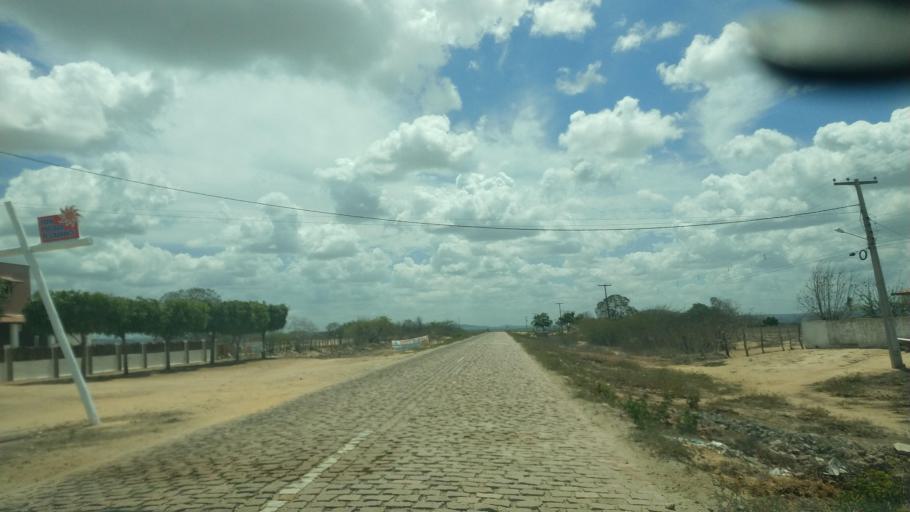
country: BR
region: Rio Grande do Norte
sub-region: Sao Paulo Do Potengi
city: Sao Paulo do Potengi
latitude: -5.9807
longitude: -35.8577
